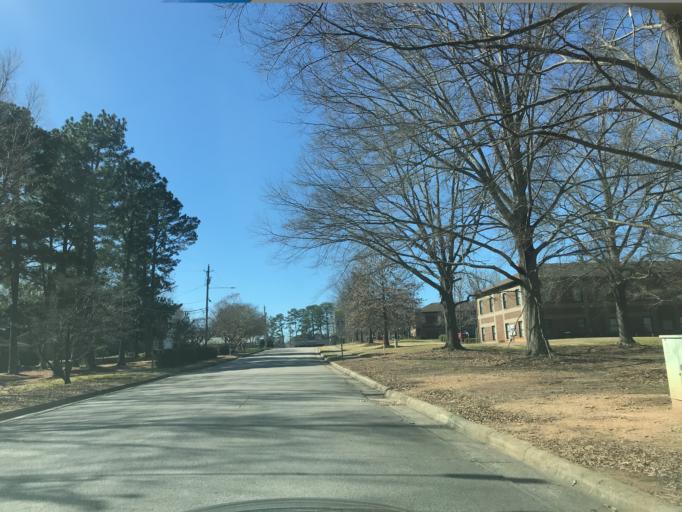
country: US
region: North Carolina
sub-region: Wake County
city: West Raleigh
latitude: 35.8531
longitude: -78.6403
